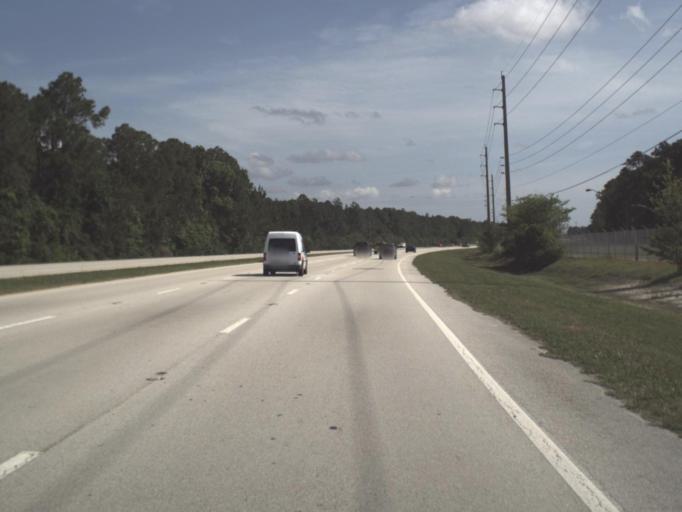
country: US
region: Florida
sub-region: Clay County
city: Orange Park
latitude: 30.2002
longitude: -81.7078
